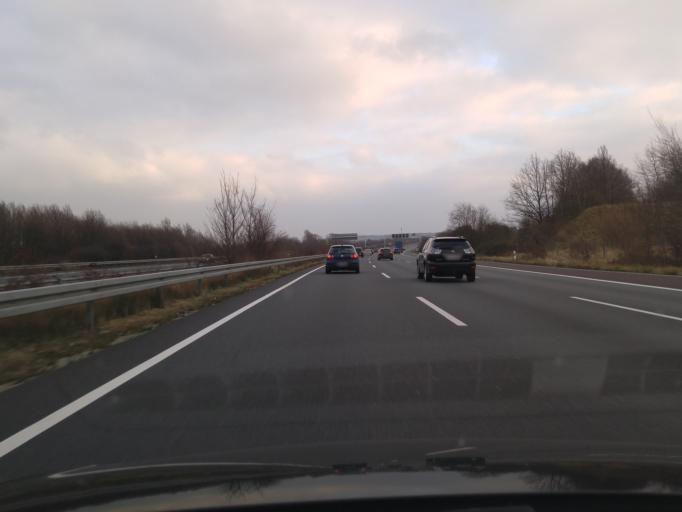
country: DE
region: Lower Saxony
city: Rennau
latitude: 52.2810
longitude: 10.9256
